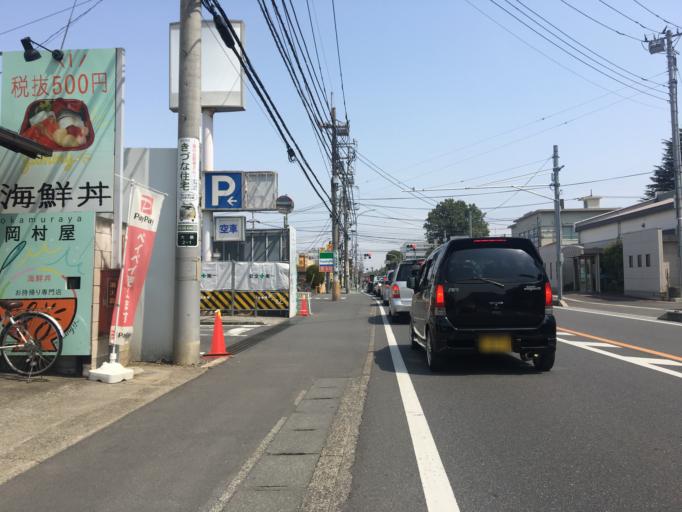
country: JP
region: Saitama
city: Kamifukuoka
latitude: 35.8799
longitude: 139.5195
